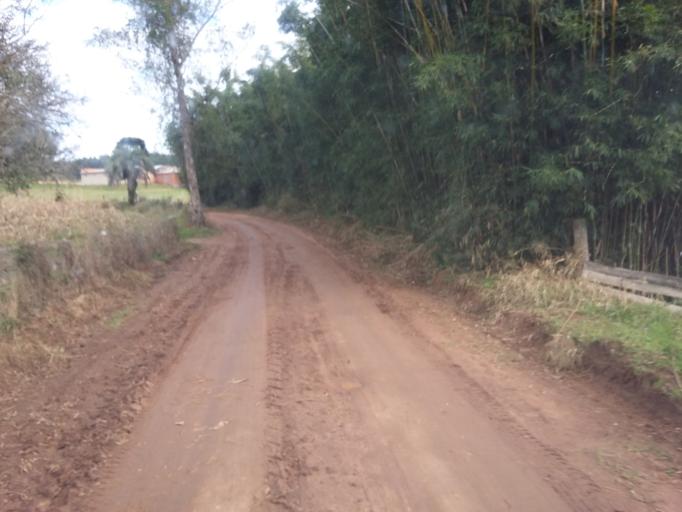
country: BR
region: Rio Grande do Sul
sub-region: Camaqua
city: Camaqua
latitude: -30.7137
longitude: -51.7847
